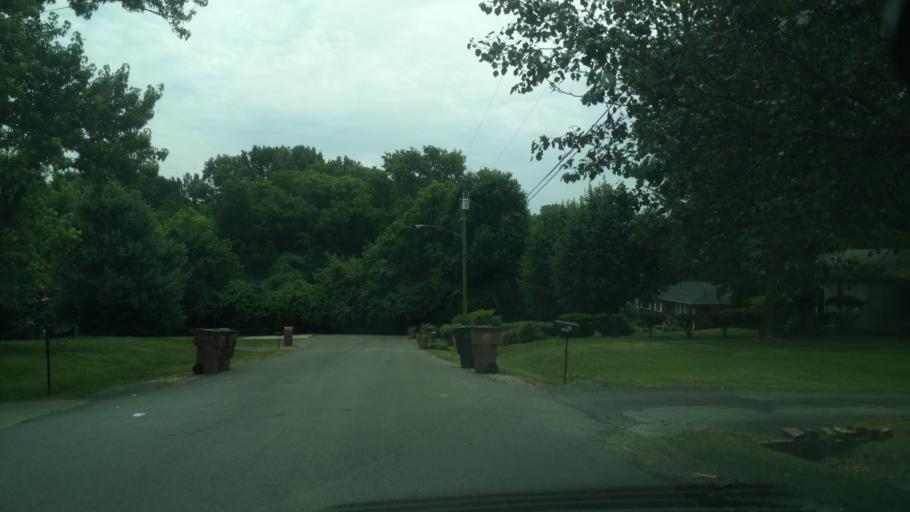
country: US
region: Tennessee
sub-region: Davidson County
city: Nashville
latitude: 36.1904
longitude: -86.7191
